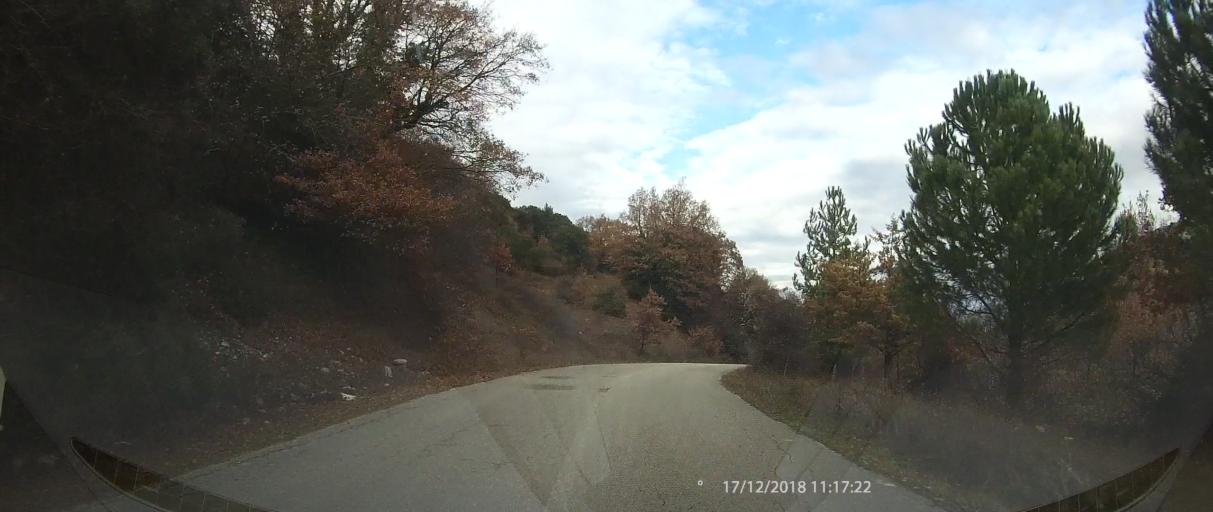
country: GR
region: Epirus
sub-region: Nomos Ioanninon
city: Kalpaki
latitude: 39.9442
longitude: 20.6633
